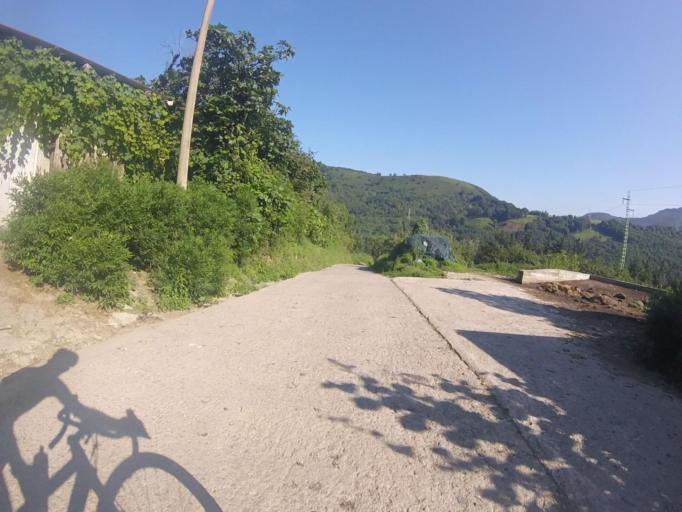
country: ES
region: Basque Country
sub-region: Provincia de Guipuzcoa
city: Astigarraga
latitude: 43.2568
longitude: -1.9407
